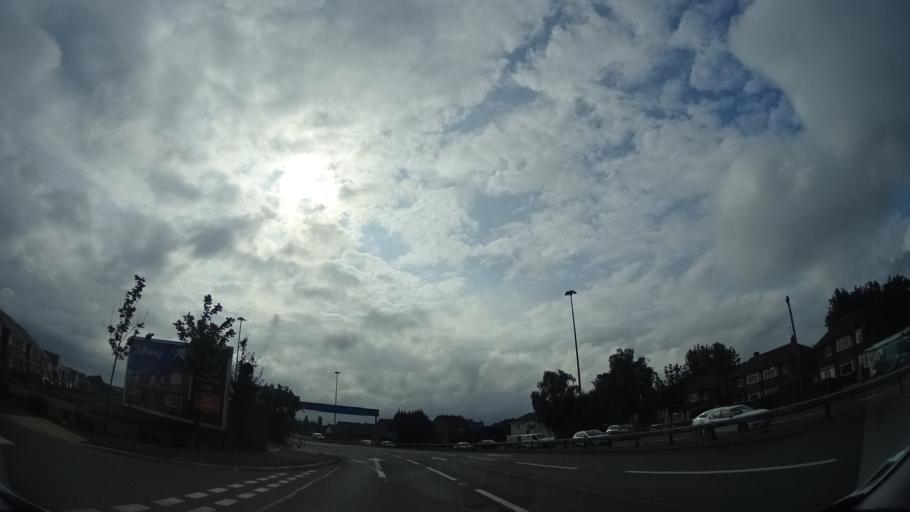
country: GB
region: England
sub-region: Knowsley
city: Huyton
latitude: 53.4063
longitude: -2.8973
